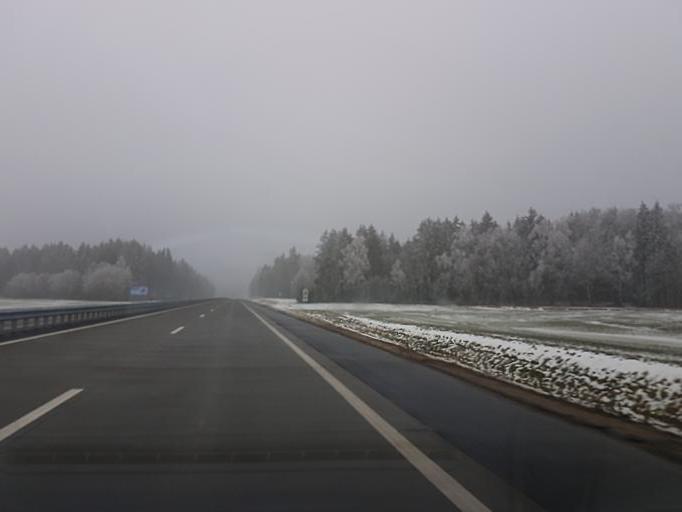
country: BY
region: Minsk
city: Atolina
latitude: 53.7172
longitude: 27.4338
